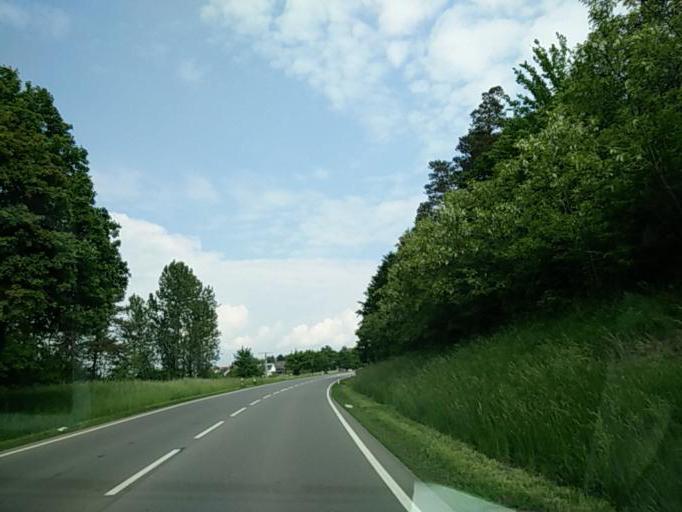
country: DE
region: Baden-Wuerttemberg
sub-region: Tuebingen Region
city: Rottenburg
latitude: 48.4438
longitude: 8.9214
